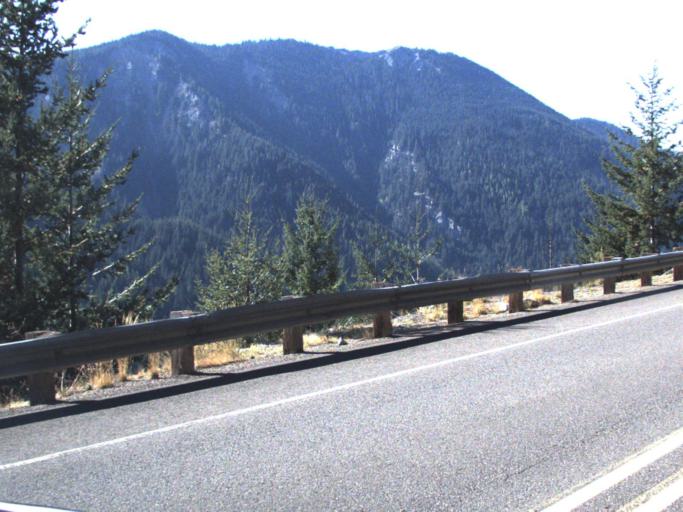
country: US
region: Washington
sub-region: Yakima County
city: Tieton
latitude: 46.6564
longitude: -121.3337
